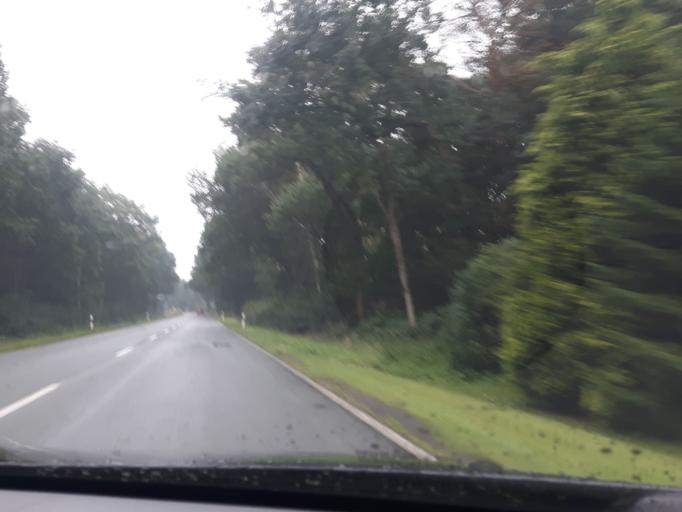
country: DE
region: Lower Saxony
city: Grossenkneten
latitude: 52.9567
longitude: 8.2120
